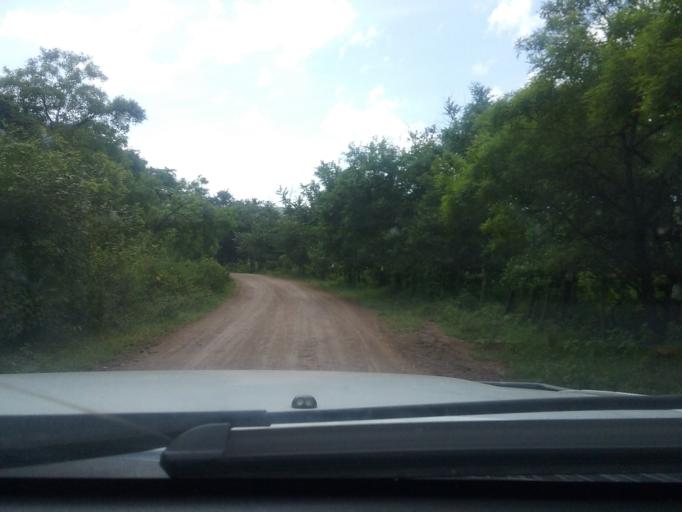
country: NI
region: Matagalpa
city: Terrabona
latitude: 12.7088
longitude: -85.9570
